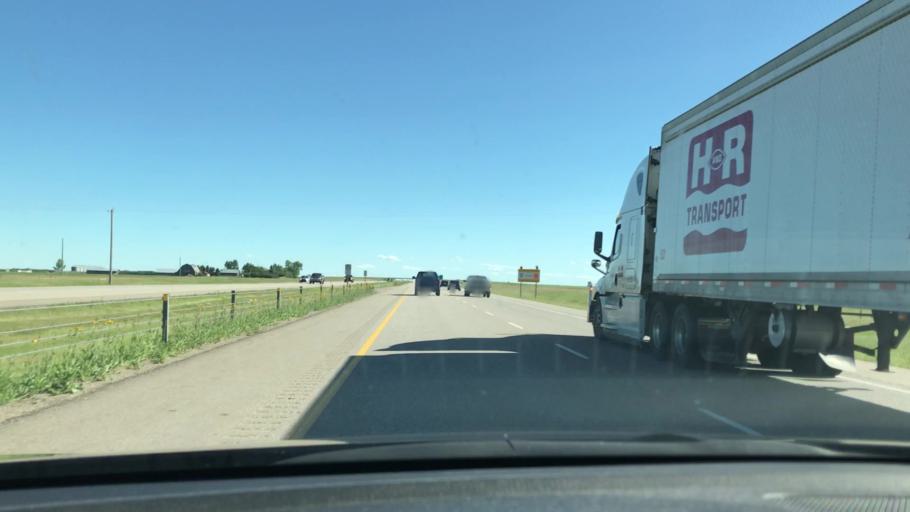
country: CA
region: Alberta
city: Didsbury
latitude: 51.6797
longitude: -114.0256
